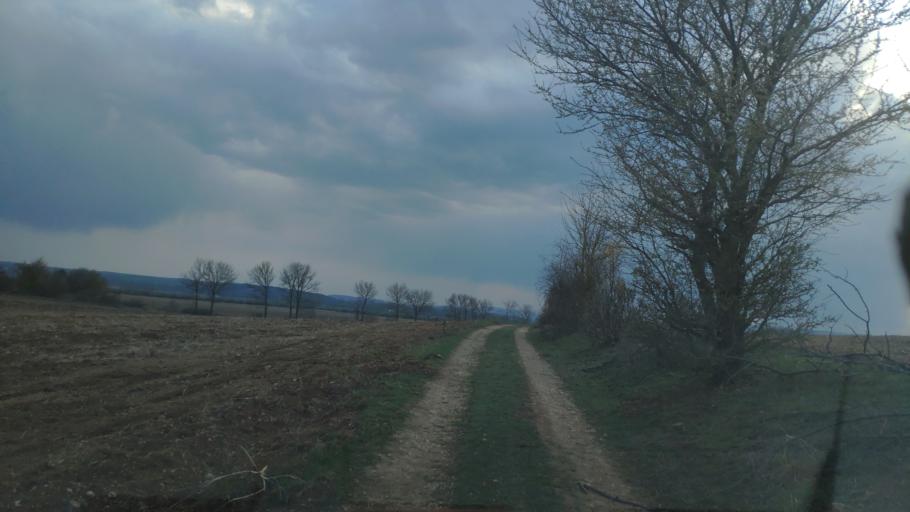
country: SK
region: Kosicky
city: Moldava nad Bodvou
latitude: 48.6187
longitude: 20.9310
